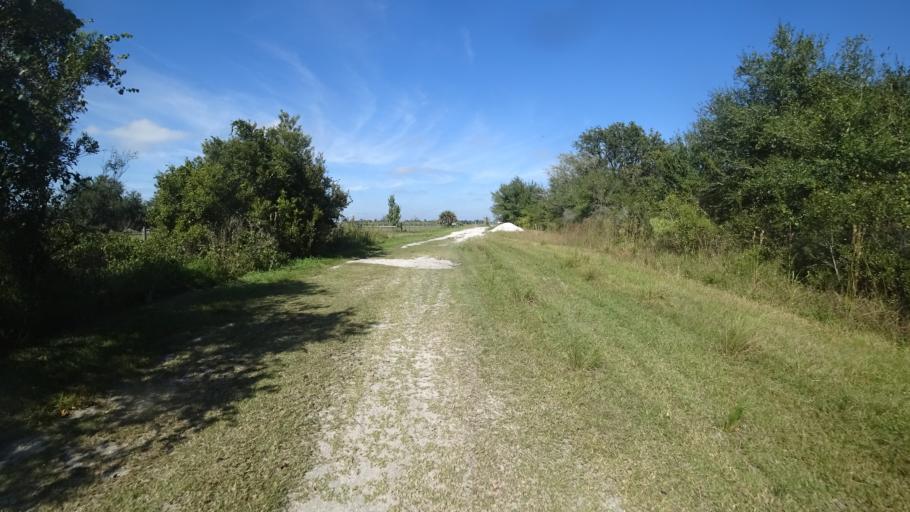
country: US
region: Florida
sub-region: DeSoto County
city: Arcadia
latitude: 27.2941
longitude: -82.0644
